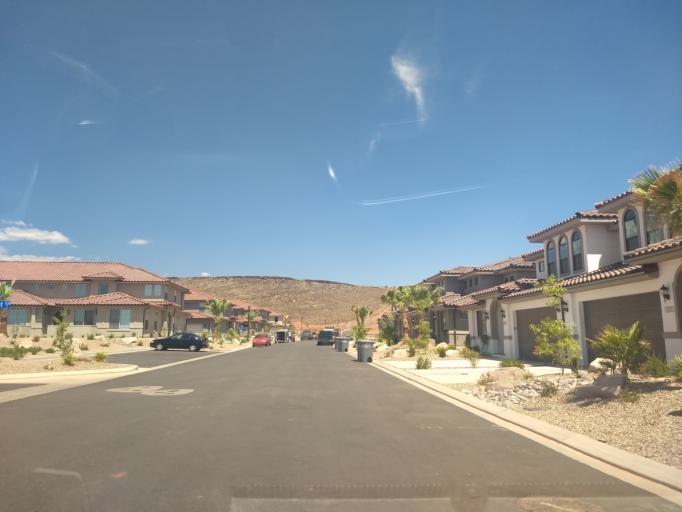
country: US
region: Utah
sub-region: Washington County
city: Washington
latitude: 37.1456
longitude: -113.4730
